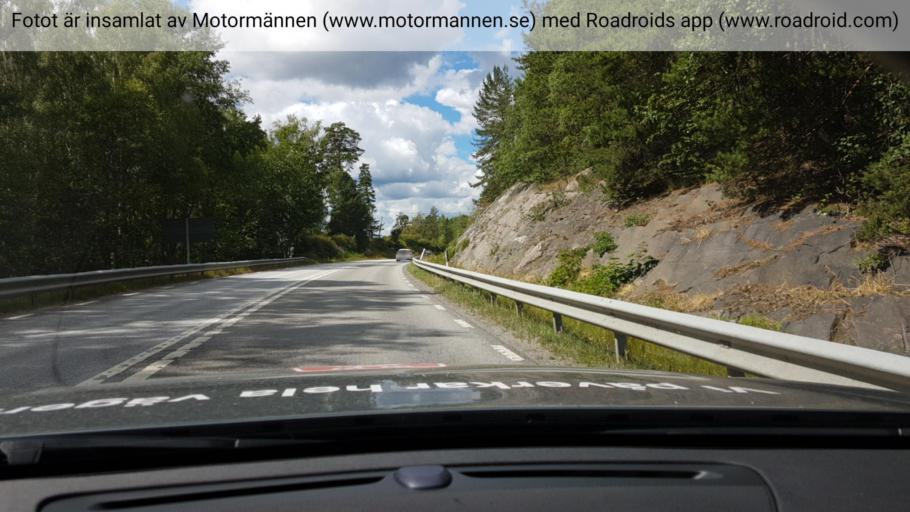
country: SE
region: Stockholm
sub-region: Vaxholms Kommun
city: Resaro
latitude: 59.4181
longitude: 18.3053
